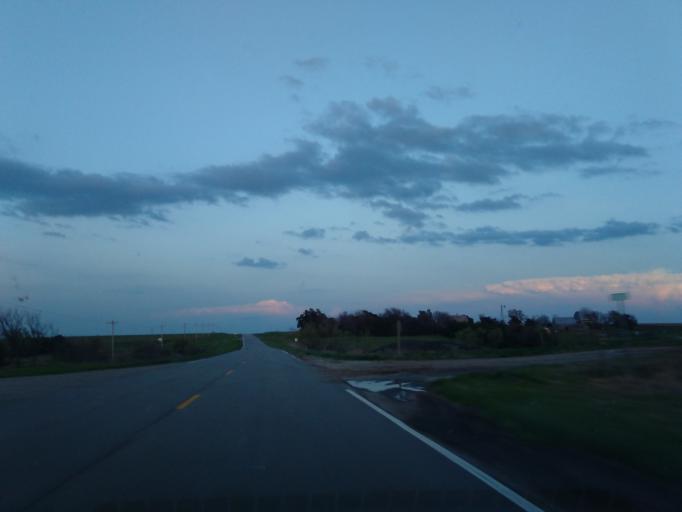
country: US
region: Nebraska
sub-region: Nuckolls County
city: Nelson
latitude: 40.2927
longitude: -98.1620
